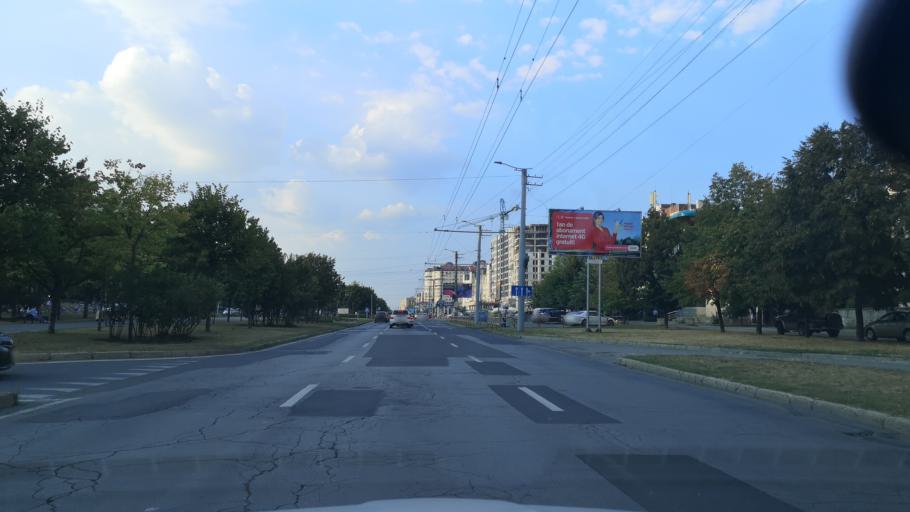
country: MD
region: Chisinau
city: Chisinau
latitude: 47.0422
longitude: 28.8904
